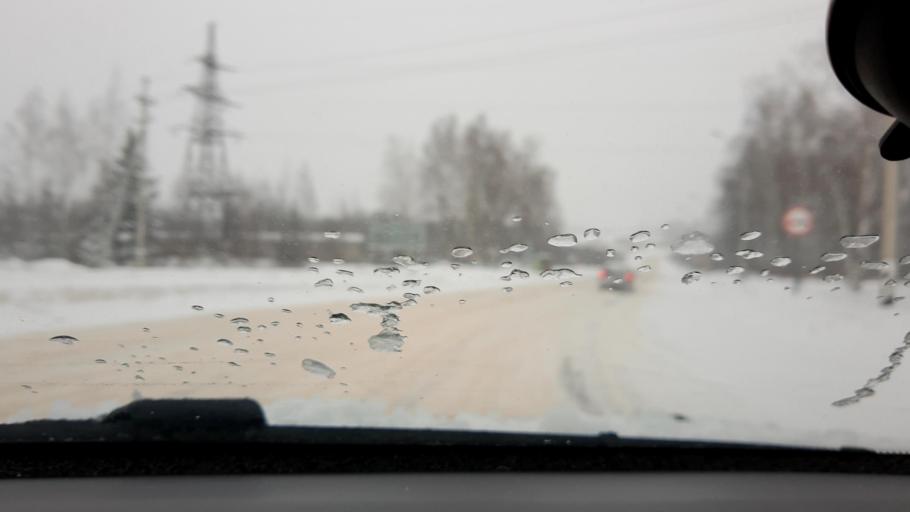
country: RU
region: Nizjnij Novgorod
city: Purekh
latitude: 56.6508
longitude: 43.0830
